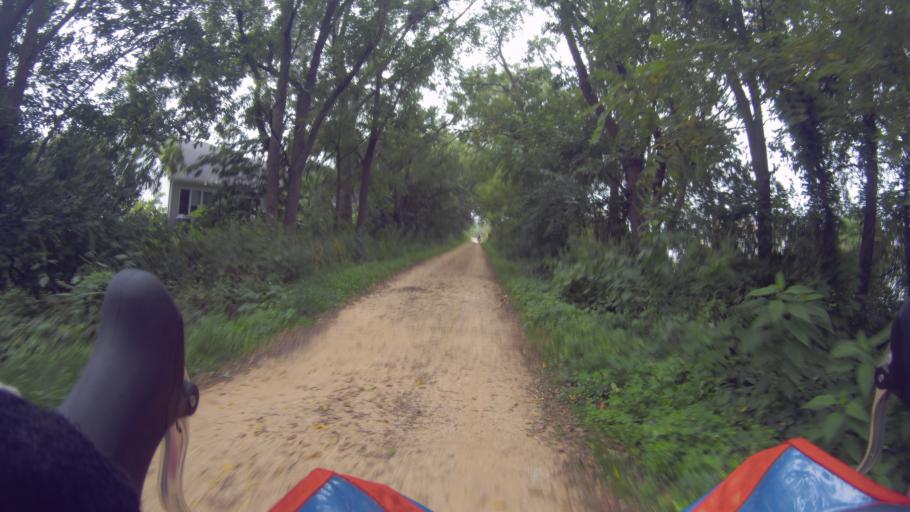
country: US
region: Wisconsin
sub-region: Dane County
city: Verona
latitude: 42.9892
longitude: -89.5308
